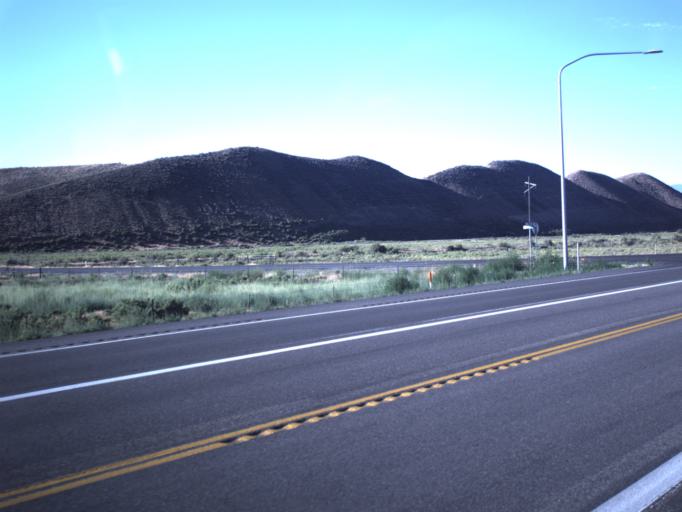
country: US
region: Utah
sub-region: Sevier County
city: Salina
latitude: 38.9432
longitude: -111.8836
